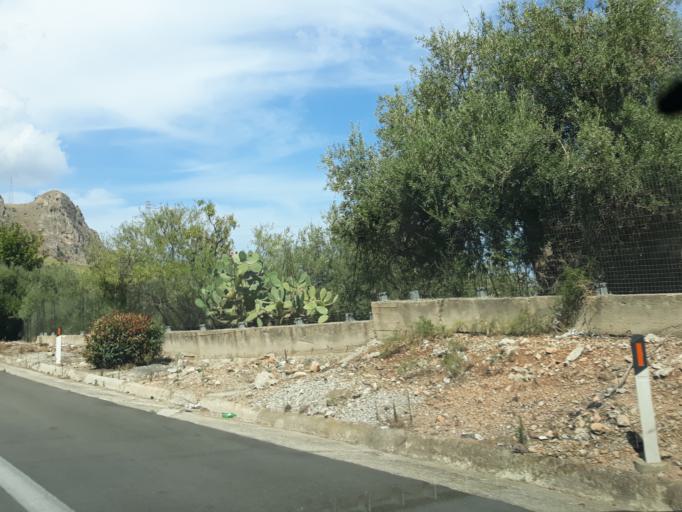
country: IT
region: Sicily
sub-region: Palermo
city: Trabia
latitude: 37.9833
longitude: 13.6609
